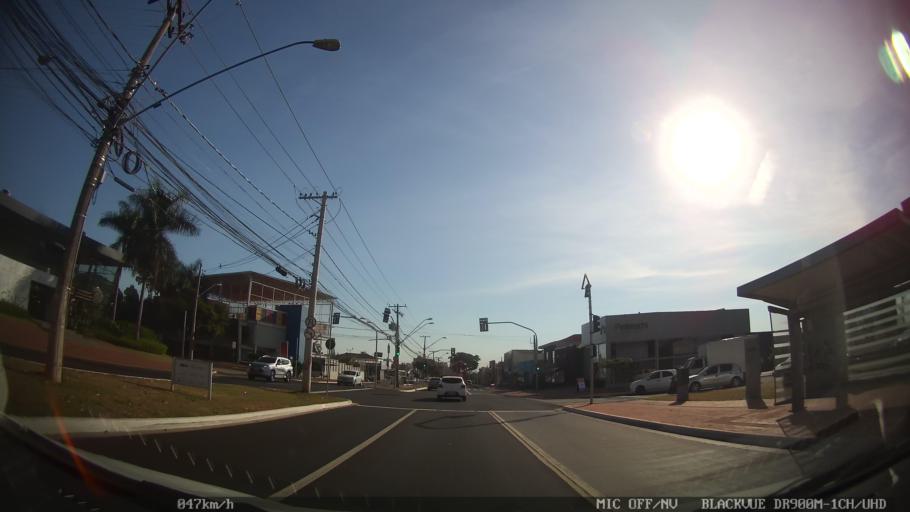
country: BR
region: Sao Paulo
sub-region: Ribeirao Preto
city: Ribeirao Preto
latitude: -21.1961
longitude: -47.8075
